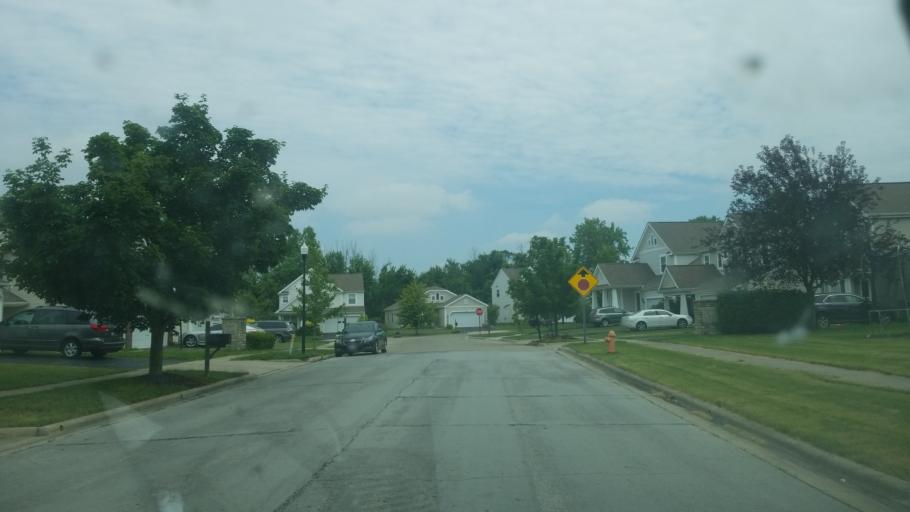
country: US
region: Ohio
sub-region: Franklin County
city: Reynoldsburg
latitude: 40.0093
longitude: -82.7855
